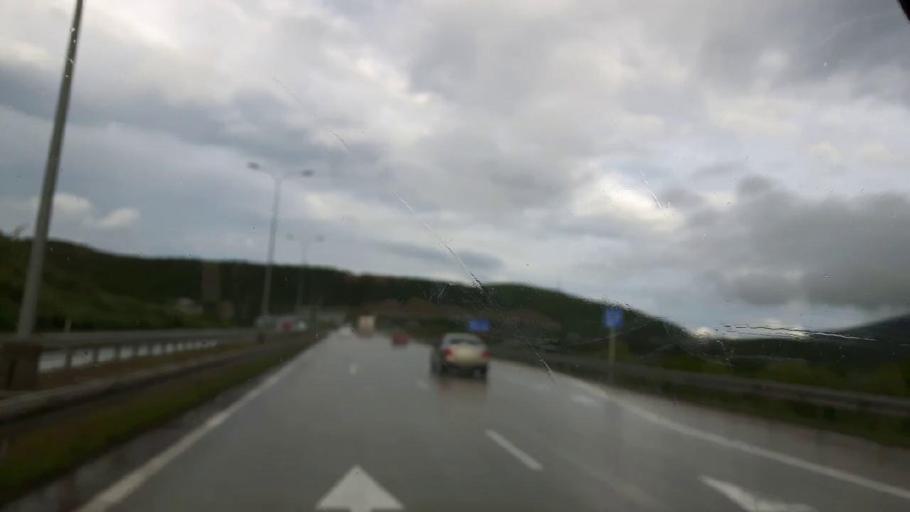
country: GE
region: Shida Kartli
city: Kaspi
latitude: 41.9956
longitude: 44.4132
